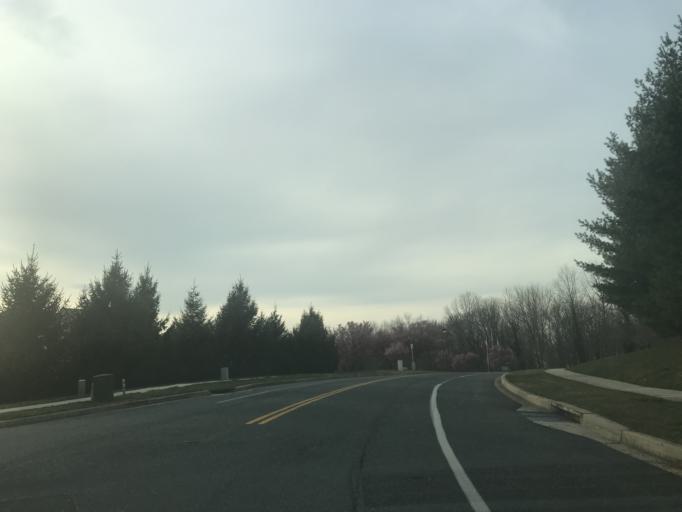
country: US
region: Maryland
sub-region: Harford County
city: South Bel Air
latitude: 39.5380
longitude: -76.3192
